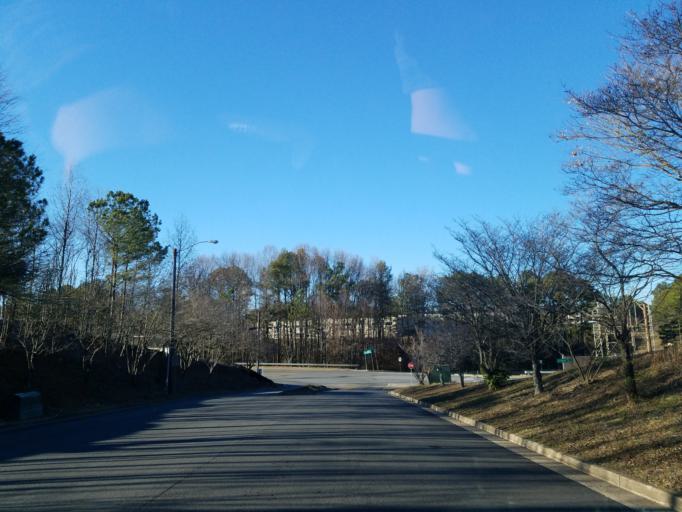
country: US
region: Georgia
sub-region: Cobb County
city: Marietta
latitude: 33.9729
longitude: -84.5275
